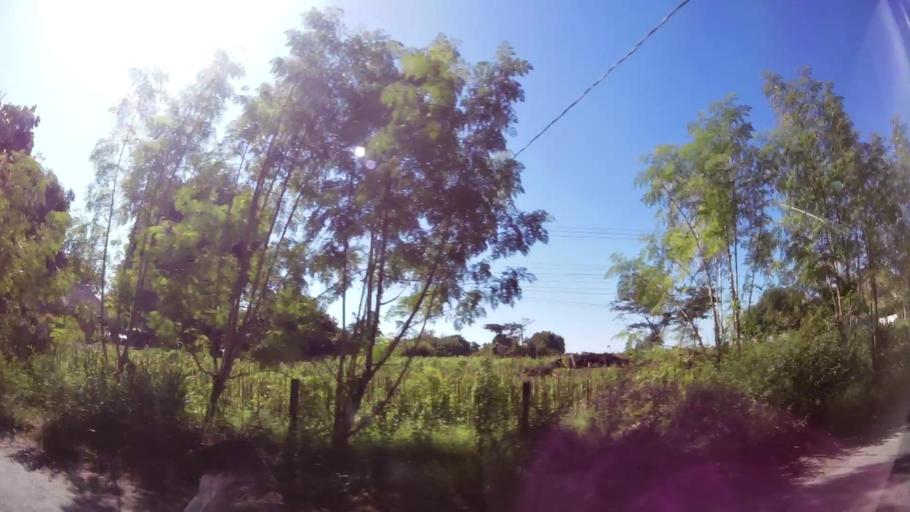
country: GT
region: Escuintla
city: Iztapa
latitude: 13.9148
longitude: -90.5453
